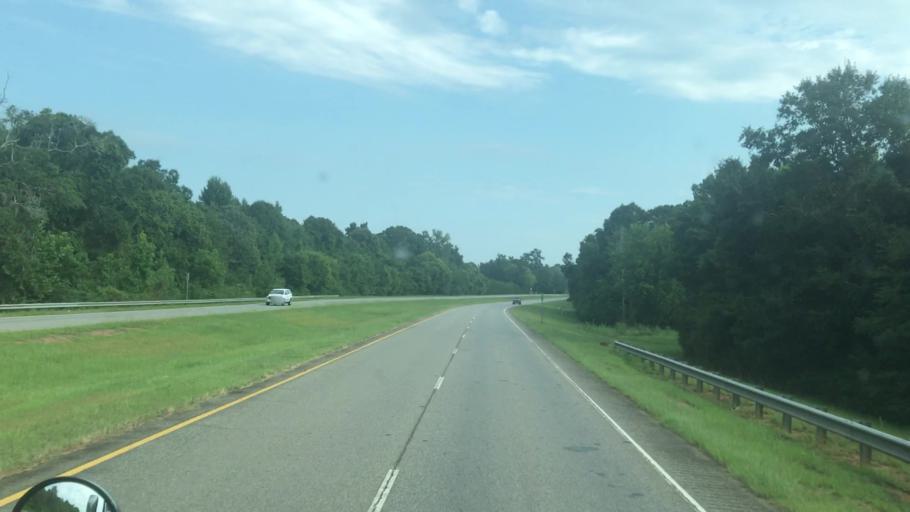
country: US
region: Georgia
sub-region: Early County
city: Blakely
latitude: 31.3696
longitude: -84.9207
